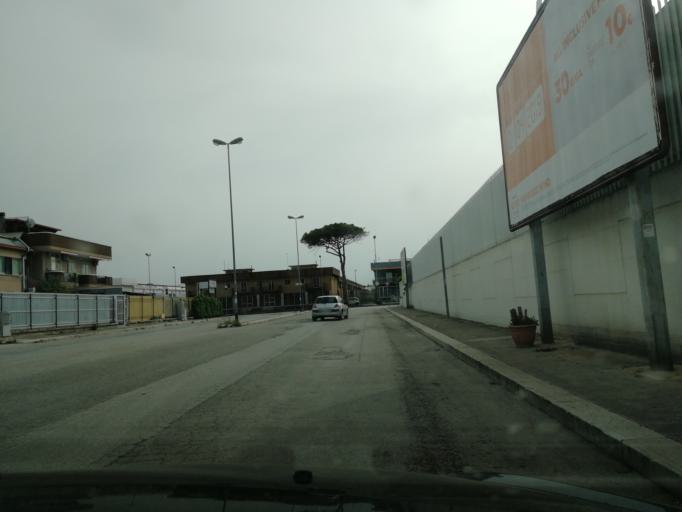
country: IT
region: Apulia
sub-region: Provincia di Barletta - Andria - Trani
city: Barletta
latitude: 41.3110
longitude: 16.3098
